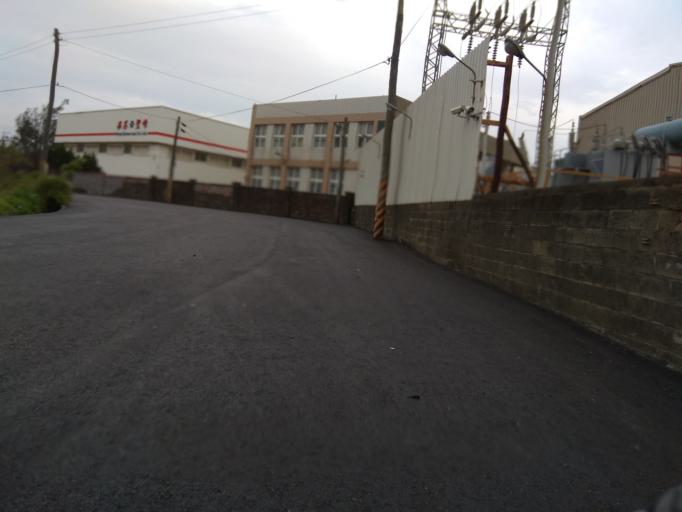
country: TW
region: Taiwan
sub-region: Hsinchu
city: Zhubei
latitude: 24.9846
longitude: 121.0355
